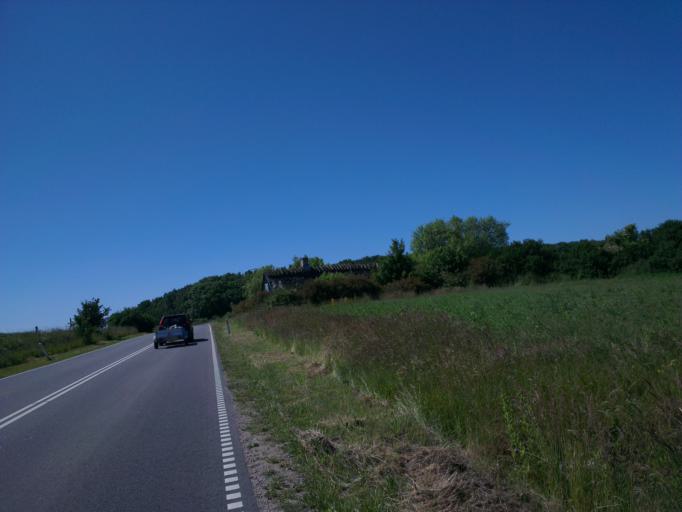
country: DK
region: Capital Region
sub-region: Frederikssund Kommune
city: Jaegerspris
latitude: 55.8794
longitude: 11.9547
